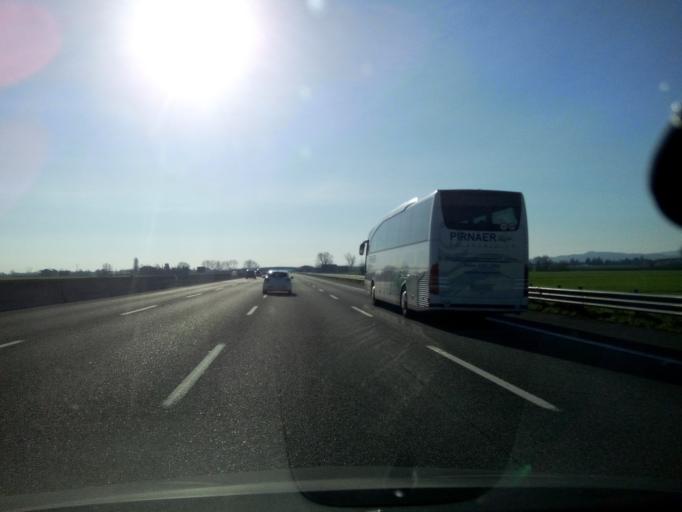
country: IT
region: Emilia-Romagna
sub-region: Provincia di Modena
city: Piumazzo
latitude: 44.5554
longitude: 11.0683
